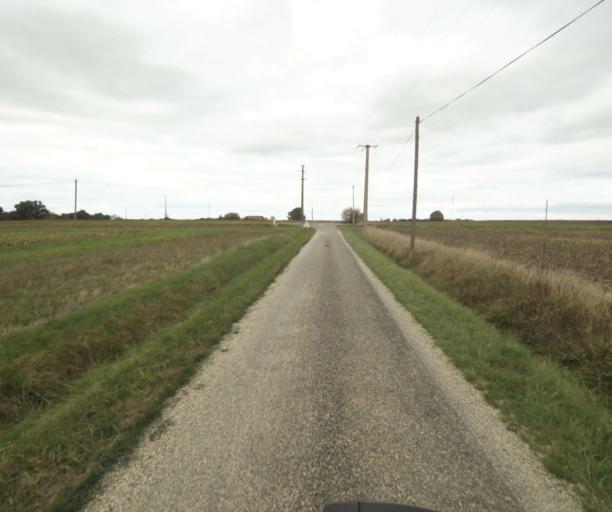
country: FR
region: Midi-Pyrenees
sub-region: Departement du Tarn-et-Garonne
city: Beaumont-de-Lomagne
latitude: 43.8641
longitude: 1.0695
